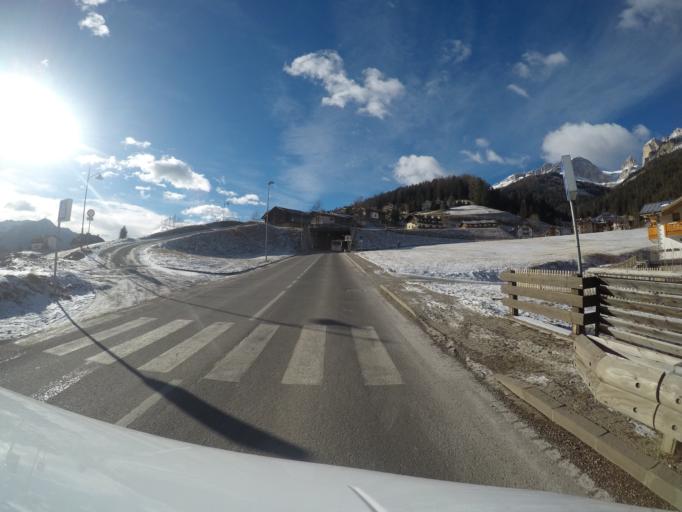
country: IT
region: Trentino-Alto Adige
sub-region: Provincia di Trento
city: Vigo di Fassa
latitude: 46.4179
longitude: 11.6728
